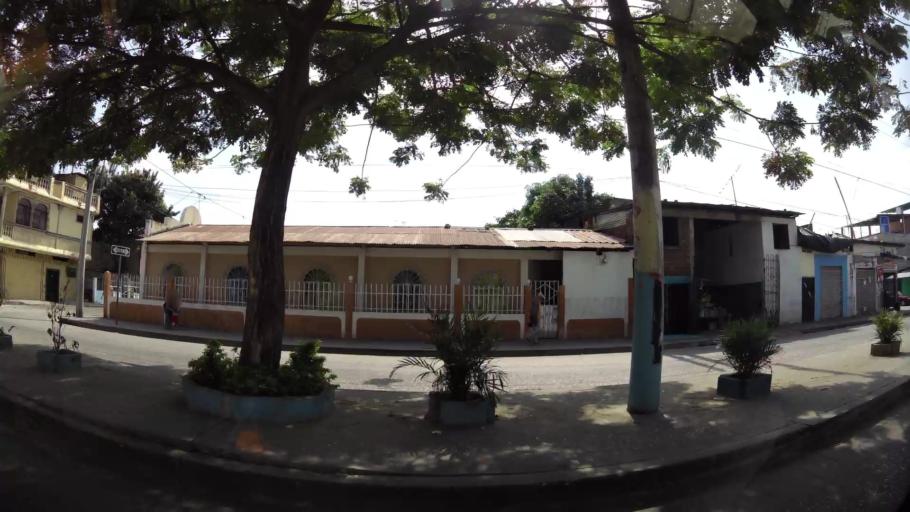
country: EC
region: Guayas
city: Guayaquil
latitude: -2.2776
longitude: -79.8846
